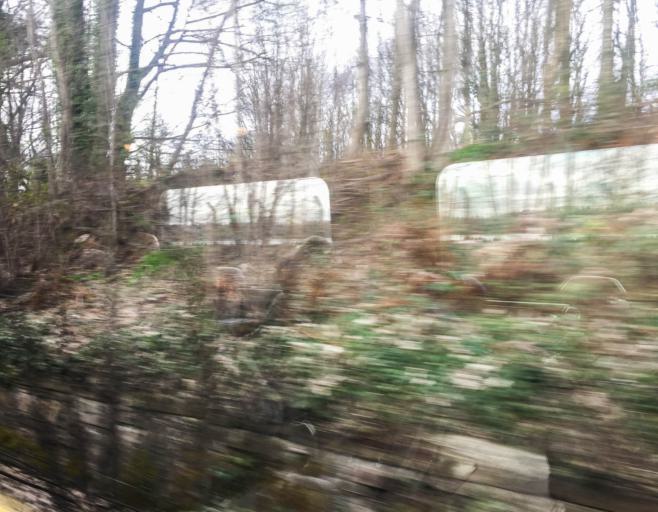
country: GB
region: Scotland
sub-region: Renfrewshire
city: Bishopton
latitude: 55.9310
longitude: -4.4976
